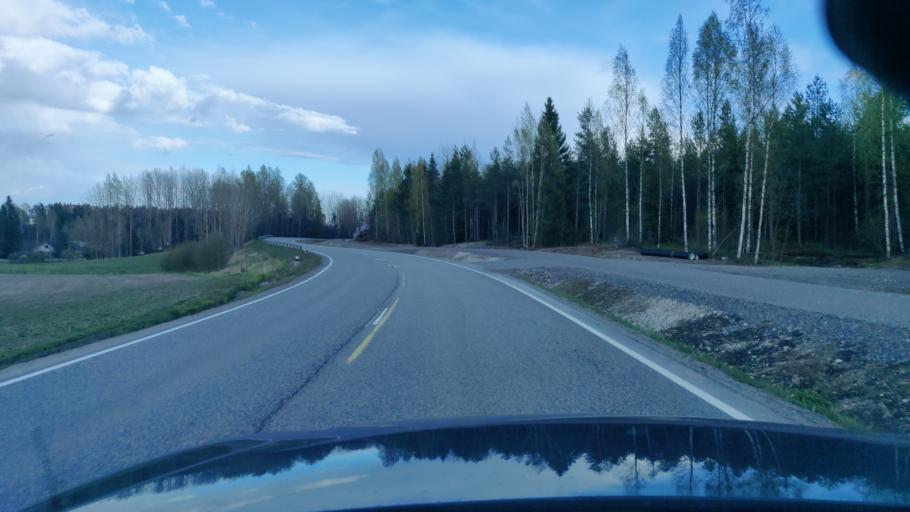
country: FI
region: Uusimaa
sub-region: Helsinki
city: Jaervenpaeae
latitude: 60.4795
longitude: 25.0602
